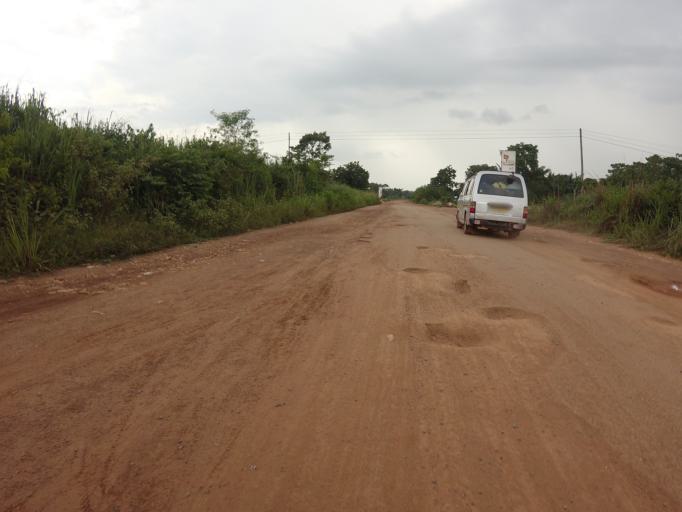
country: GH
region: Volta
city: Kpandu
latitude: 7.0048
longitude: 0.4324
